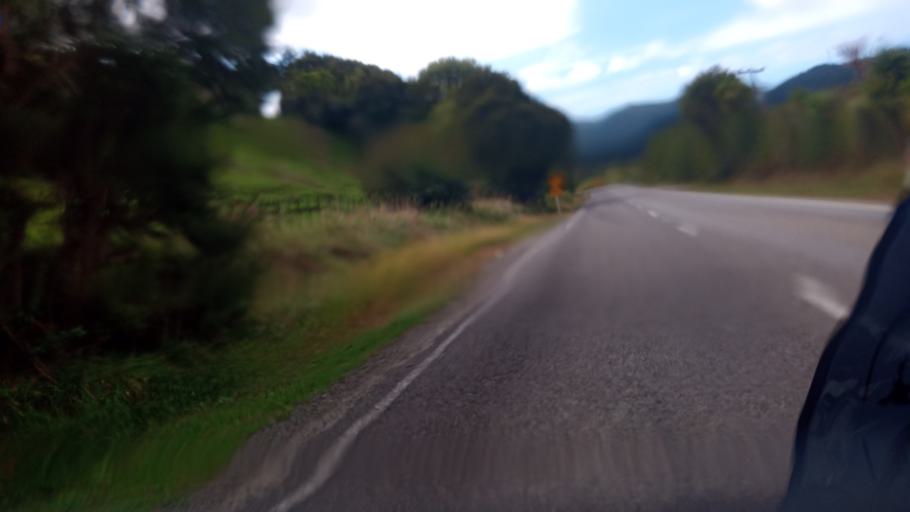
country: NZ
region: Gisborne
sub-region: Gisborne District
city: Gisborne
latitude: -38.2234
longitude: 178.2564
